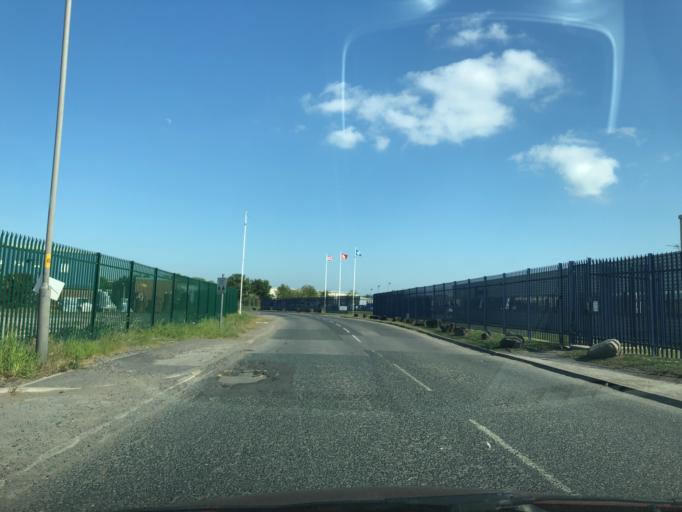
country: GB
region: England
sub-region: North Yorkshire
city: Thirsk
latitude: 54.1724
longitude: -1.3652
